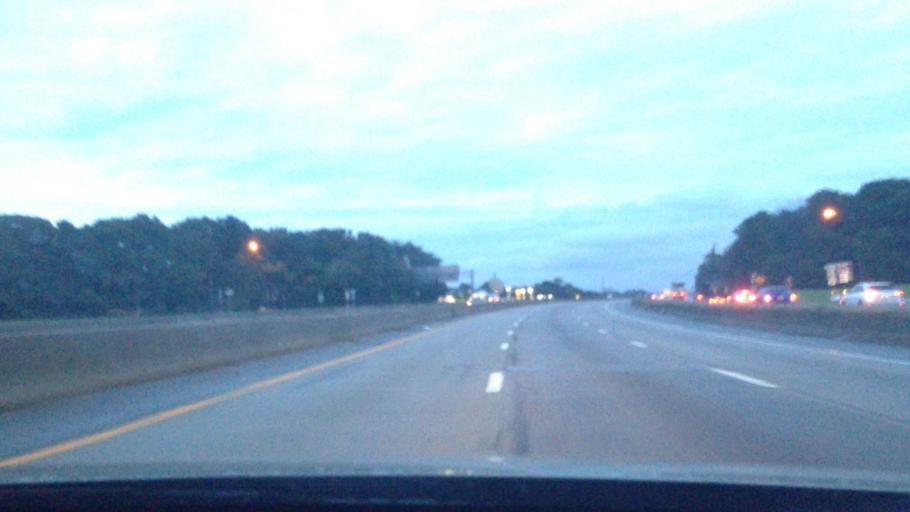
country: US
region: New York
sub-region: Suffolk County
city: North Great River
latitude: 40.7458
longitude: -73.1783
